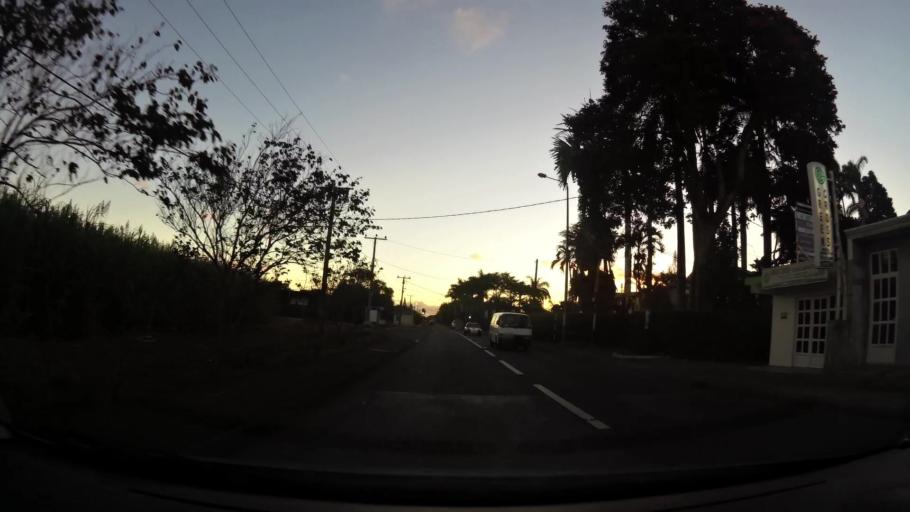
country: MU
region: Moka
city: Saint Pierre
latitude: -20.2237
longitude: 57.5185
